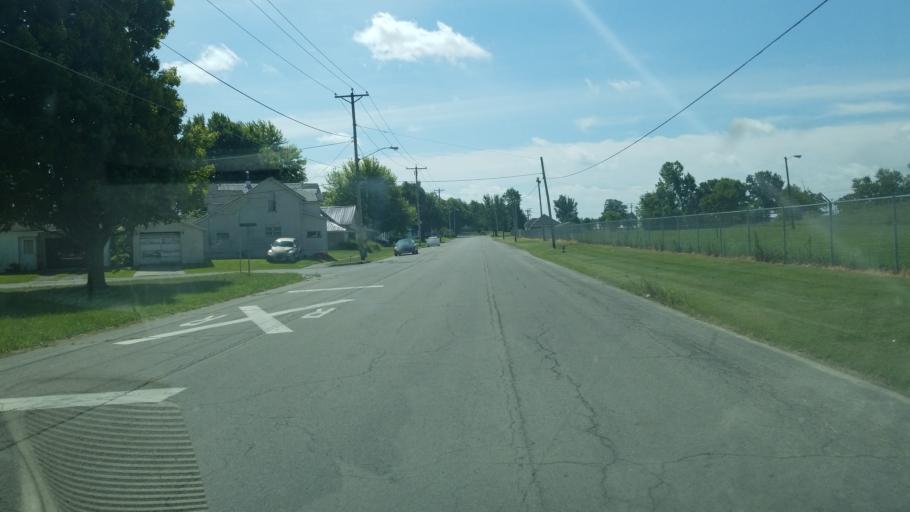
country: US
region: Ohio
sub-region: Hardin County
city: Kenton
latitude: 40.6360
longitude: -83.6083
